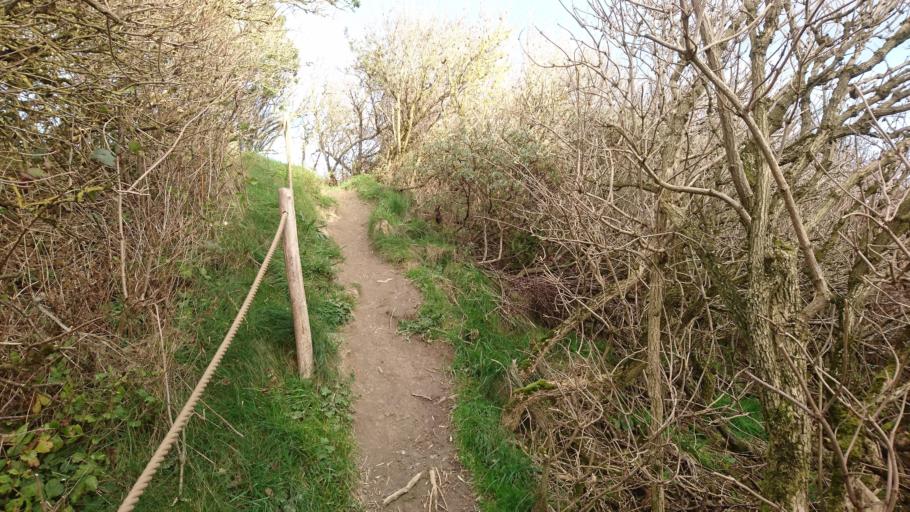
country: DK
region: North Denmark
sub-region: Morso Kommune
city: Nykobing Mors
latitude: 56.8376
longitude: 8.9628
